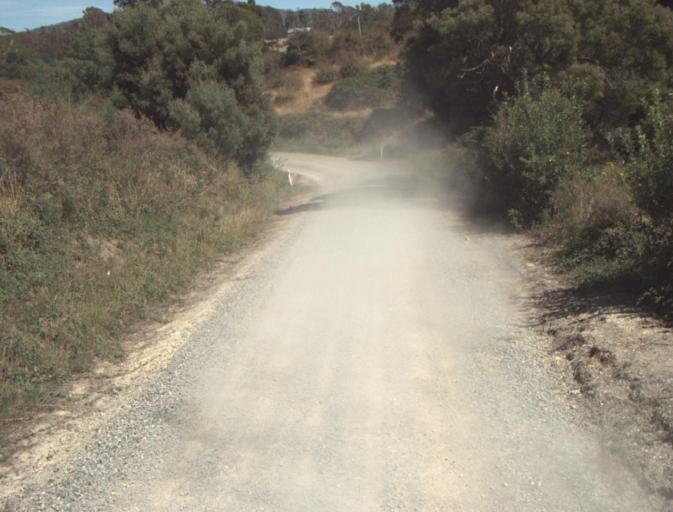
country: AU
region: Tasmania
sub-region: Launceston
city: Mayfield
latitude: -41.2568
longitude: 147.1712
